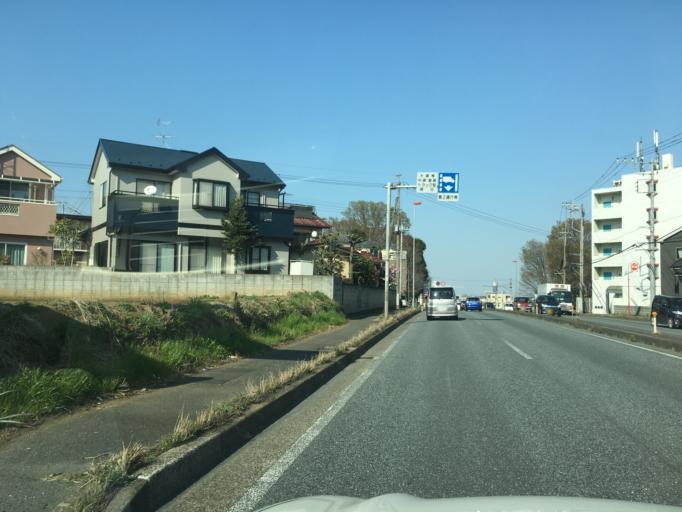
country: JP
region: Saitama
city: Kawagoe
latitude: 35.9047
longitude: 139.4911
